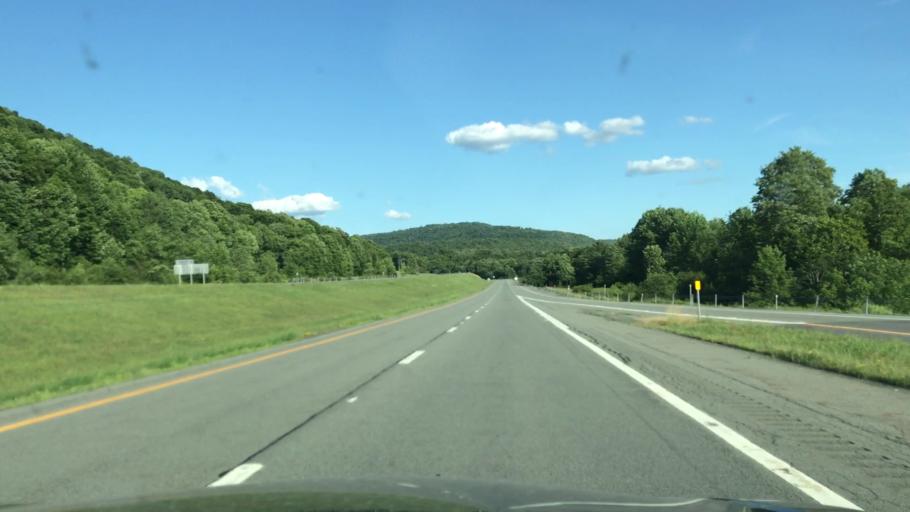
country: US
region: New York
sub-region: Sullivan County
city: Livingston Manor
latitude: 41.9566
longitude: -74.9878
